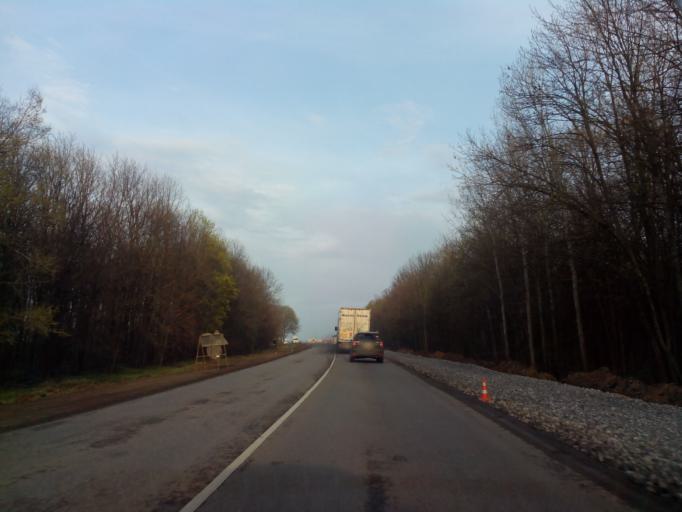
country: RU
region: Rjazan
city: Zarechnyy
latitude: 53.7529
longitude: 39.7992
